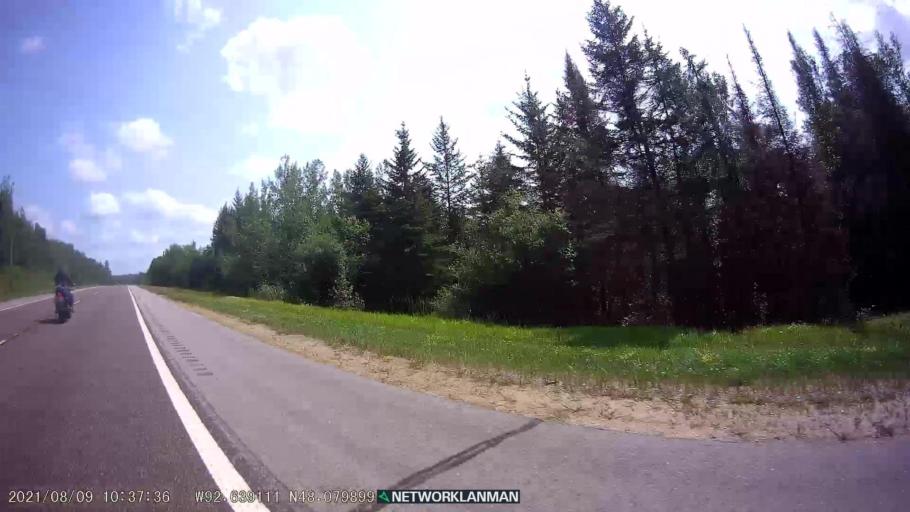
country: US
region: Minnesota
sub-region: Saint Louis County
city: Mountain Iron
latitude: 48.0812
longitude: -92.6373
